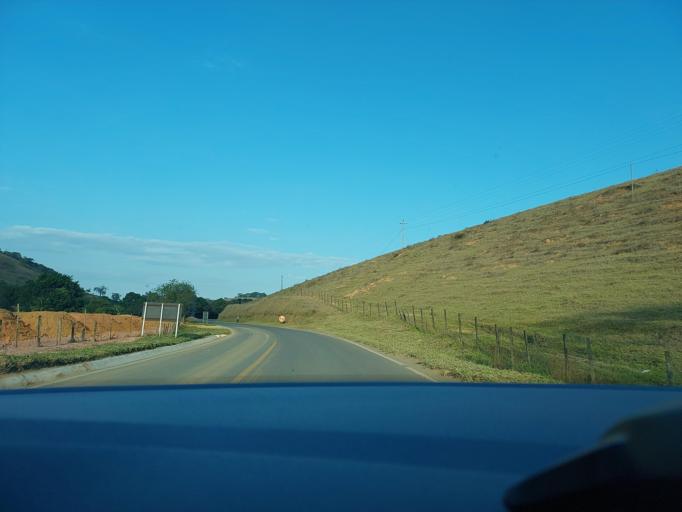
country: BR
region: Minas Gerais
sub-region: Muriae
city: Muriae
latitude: -21.1140
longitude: -42.4356
